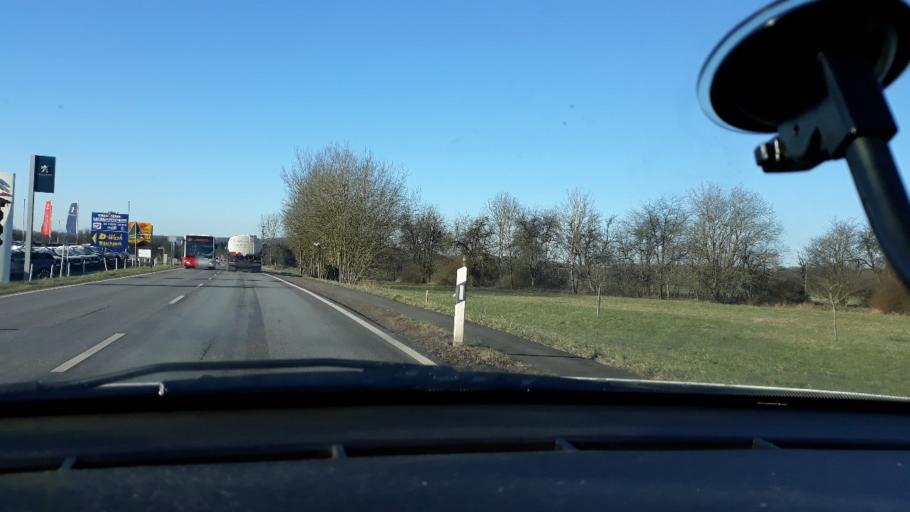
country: DE
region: Saarland
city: Gersheim
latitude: 49.2128
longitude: 7.1815
